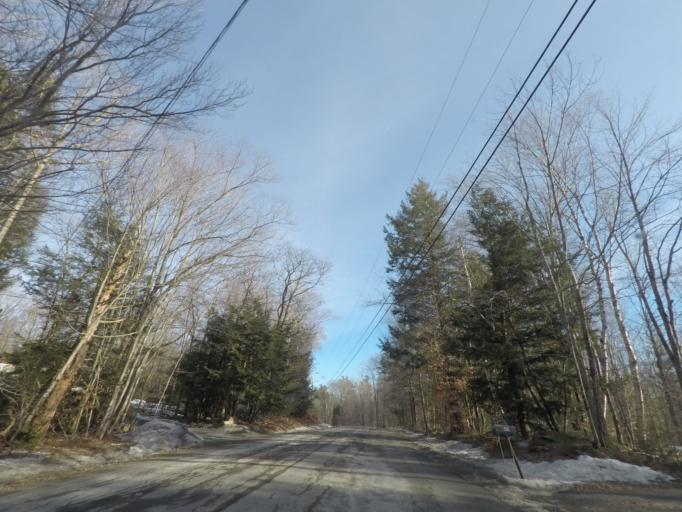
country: US
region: New York
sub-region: Rensselaer County
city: Hoosick Falls
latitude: 42.7401
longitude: -73.3944
